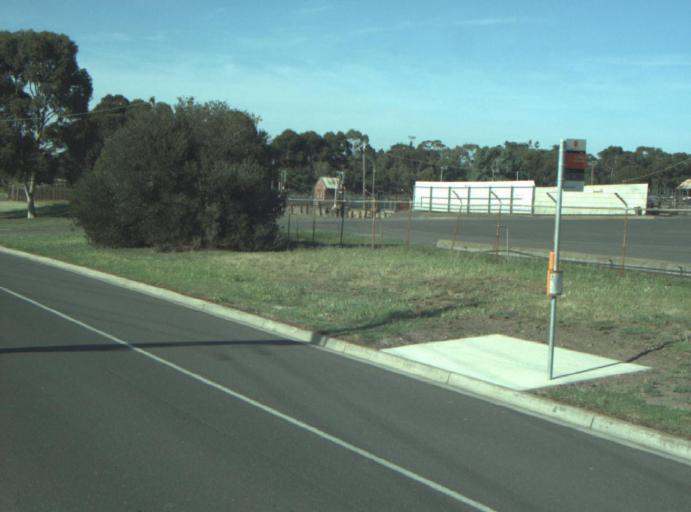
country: AU
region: Victoria
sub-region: Greater Geelong
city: Geelong West
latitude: -38.1257
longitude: 144.3464
